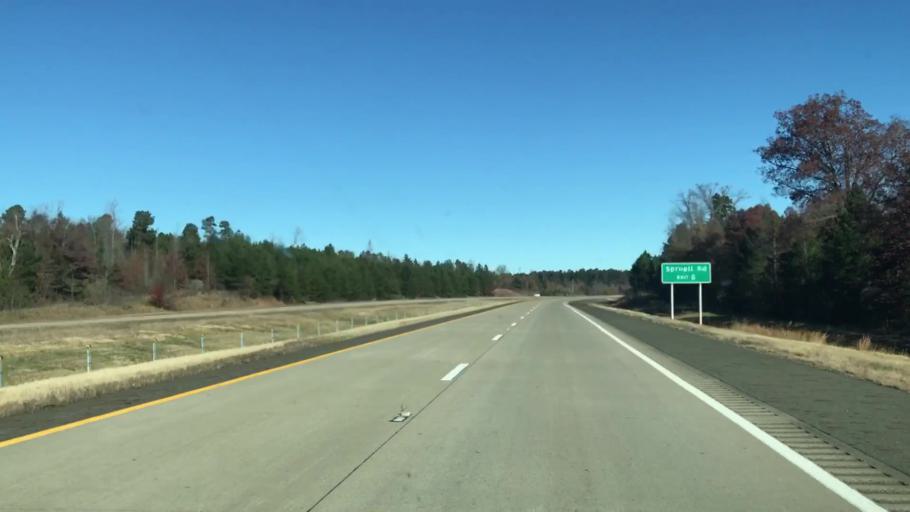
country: US
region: Louisiana
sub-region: Caddo Parish
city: Vivian
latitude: 33.1036
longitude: -93.8957
